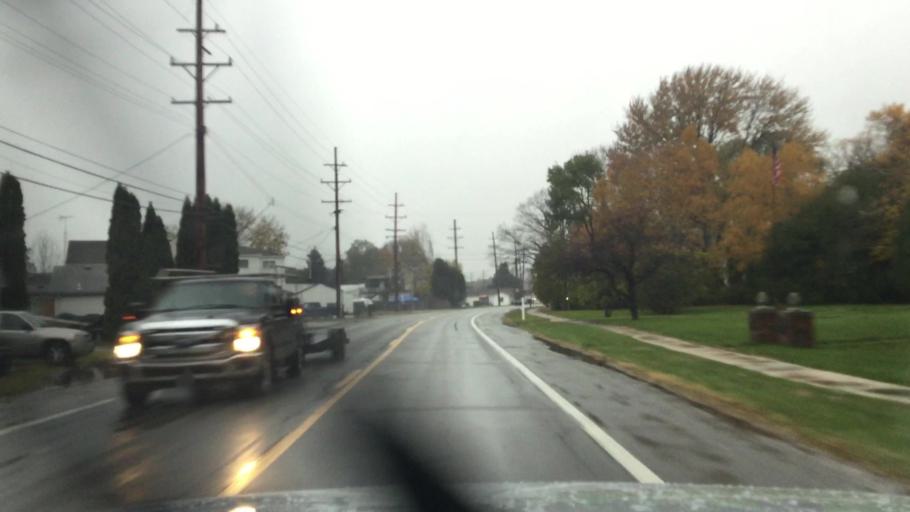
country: US
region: Michigan
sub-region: Saint Clair County
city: Algonac
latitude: 42.6195
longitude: -82.5637
